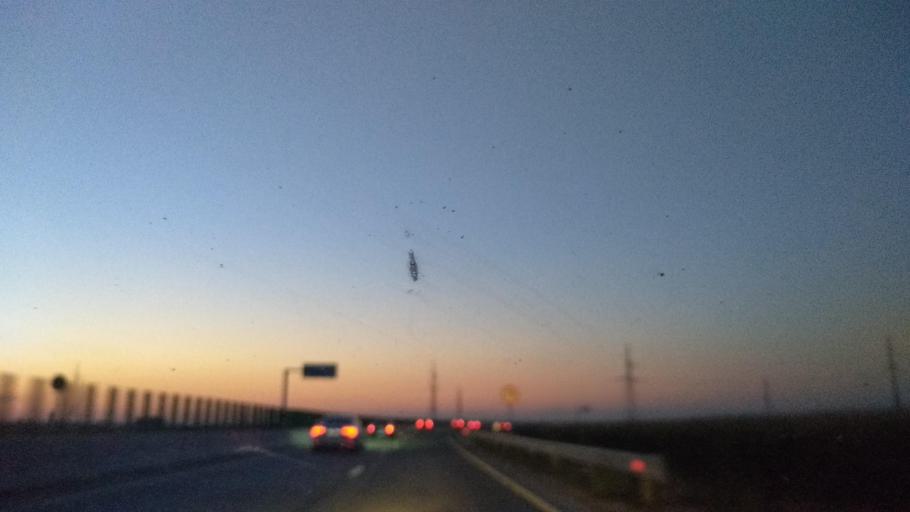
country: RO
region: Giurgiu
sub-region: Comuna Fratesti
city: Remus
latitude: 43.9555
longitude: 25.9842
